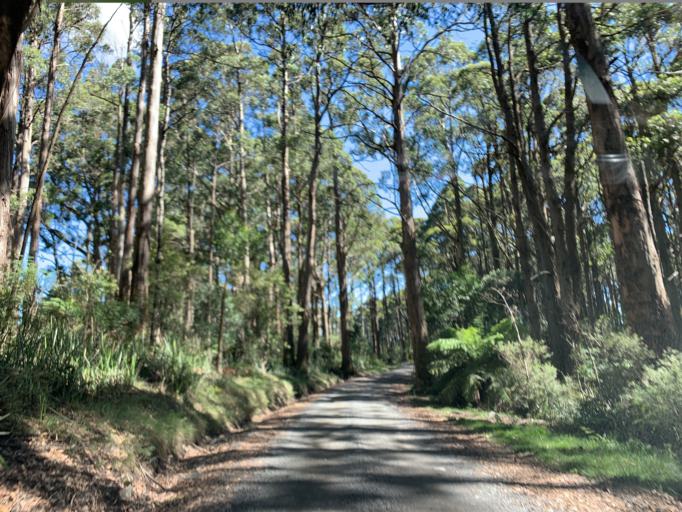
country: AU
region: Victoria
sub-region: Yarra Ranges
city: Millgrove
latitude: -37.7208
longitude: 145.6174
